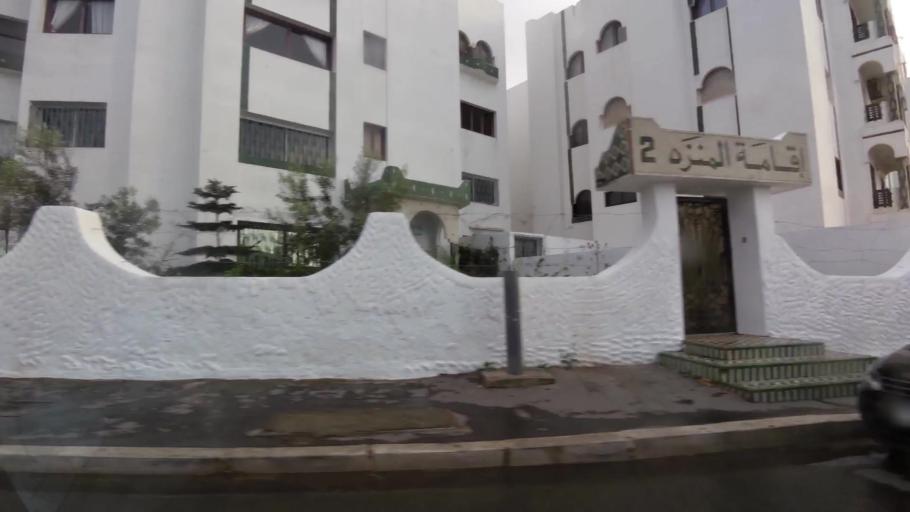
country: MA
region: Grand Casablanca
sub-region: Casablanca
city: Casablanca
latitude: 33.5828
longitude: -7.6764
